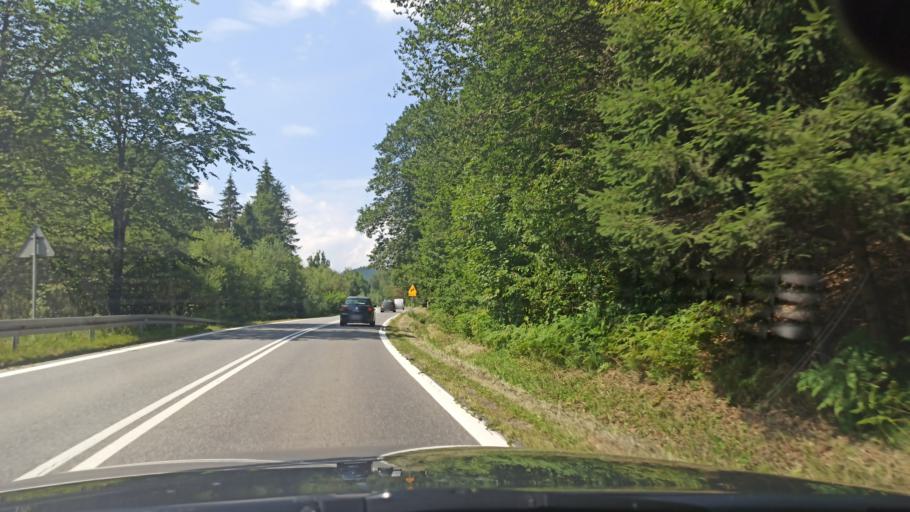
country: PL
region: Lesser Poland Voivodeship
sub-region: Powiat nowotarski
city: Krosnica
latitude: 49.4427
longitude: 20.3509
